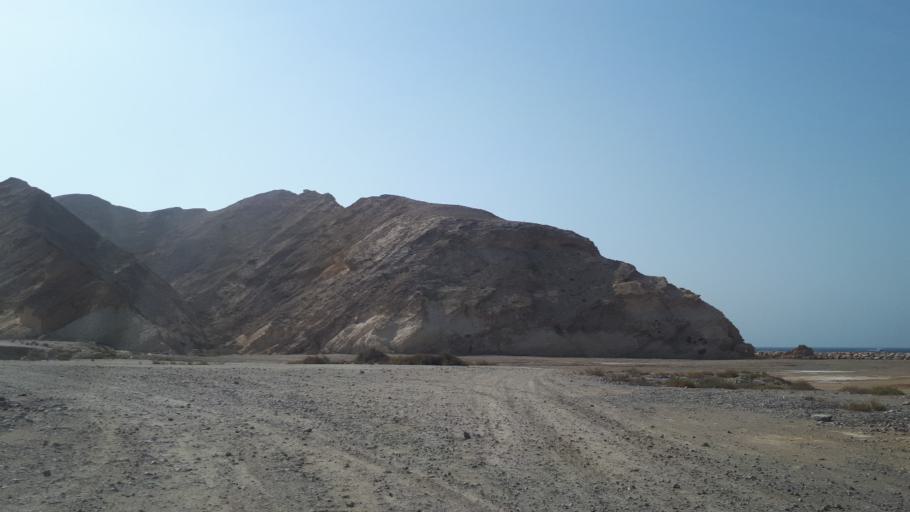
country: OM
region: Muhafazat Masqat
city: Muscat
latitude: 23.5440
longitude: 58.6677
